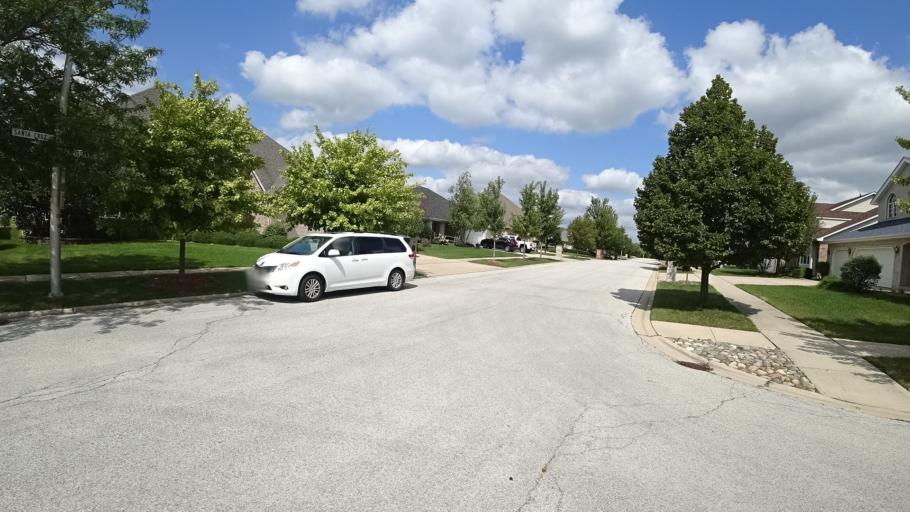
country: US
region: Illinois
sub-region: Cook County
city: Orland Hills
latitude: 41.5714
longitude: -87.8743
